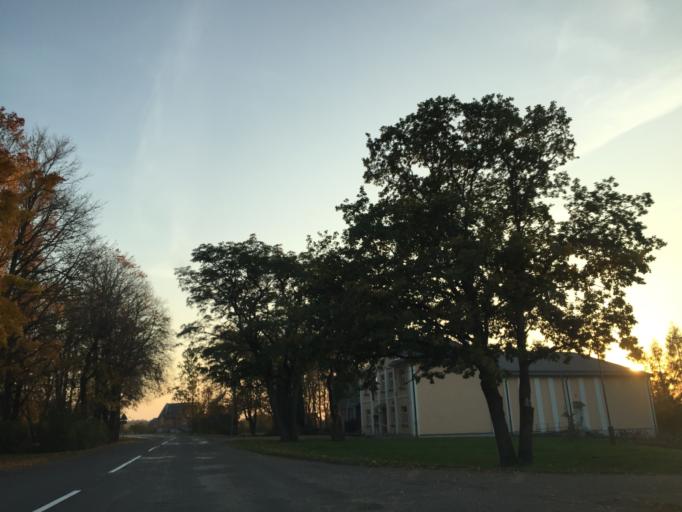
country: LV
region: Priekule
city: Priekule
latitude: 56.3684
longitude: 21.6039
